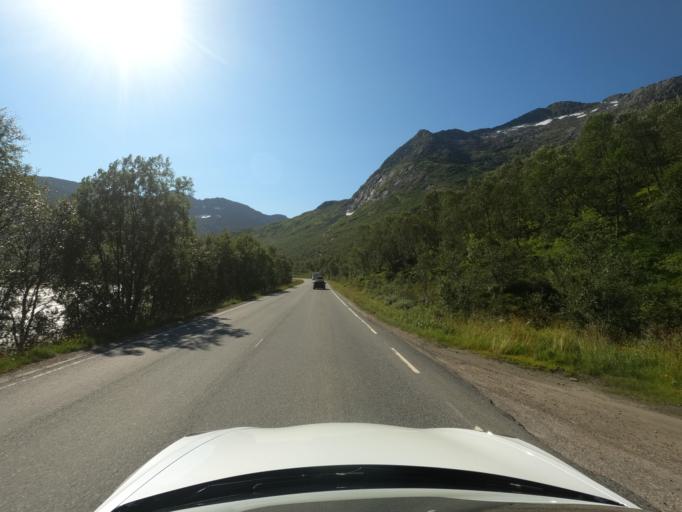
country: NO
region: Nordland
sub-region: Lodingen
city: Lodingen
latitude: 68.5347
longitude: 15.7233
